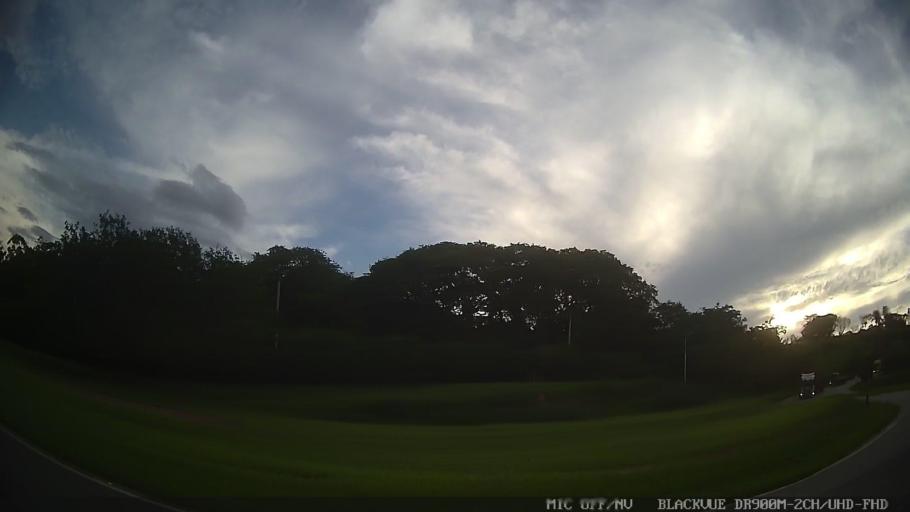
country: BR
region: Sao Paulo
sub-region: Porto Feliz
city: Porto Feliz
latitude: -23.2263
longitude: -47.5690
